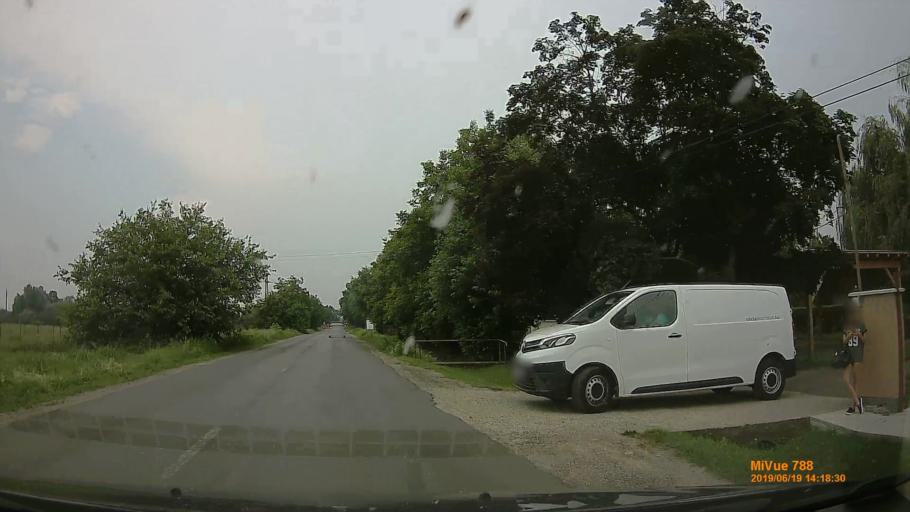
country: HU
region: Baranya
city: Szigetvar
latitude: 46.0417
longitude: 17.7820
